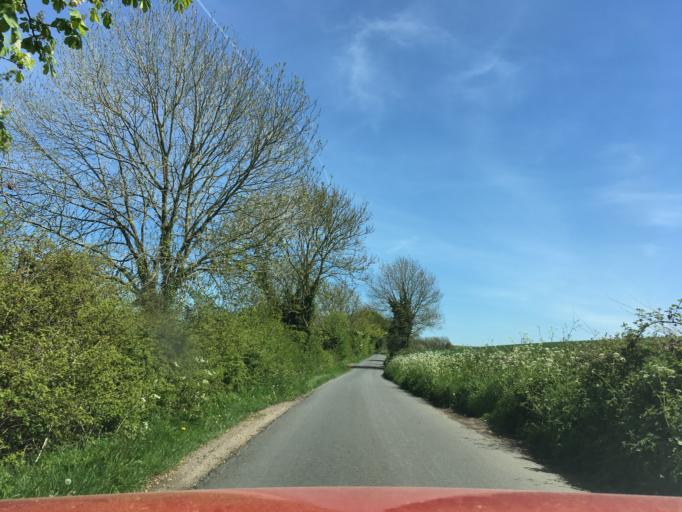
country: GB
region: England
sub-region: Gloucestershire
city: Chalford
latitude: 51.7231
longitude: -2.1105
